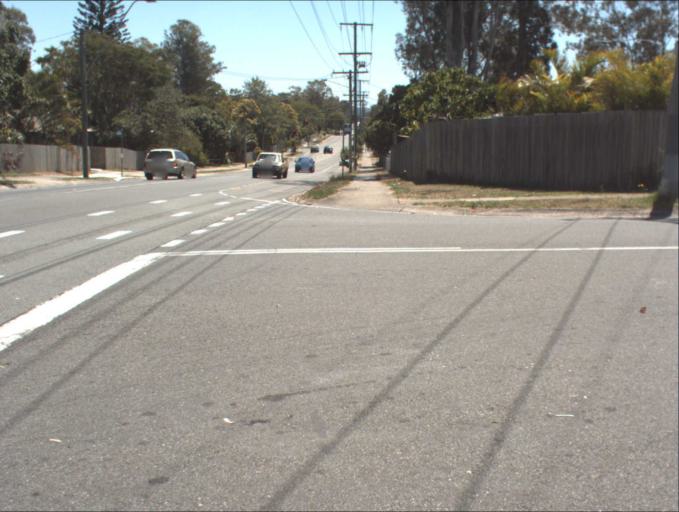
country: AU
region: Queensland
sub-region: Gold Coast
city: Yatala
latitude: -27.7116
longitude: 153.2115
